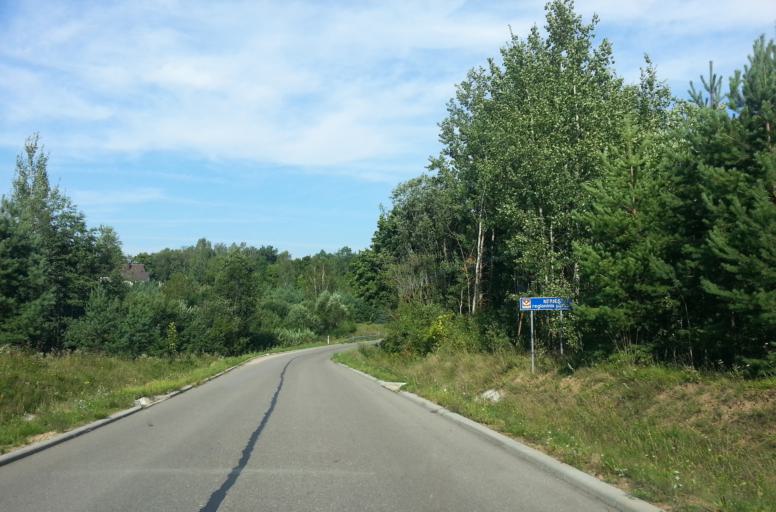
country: LT
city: Grigiskes
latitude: 54.7263
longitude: 25.0719
